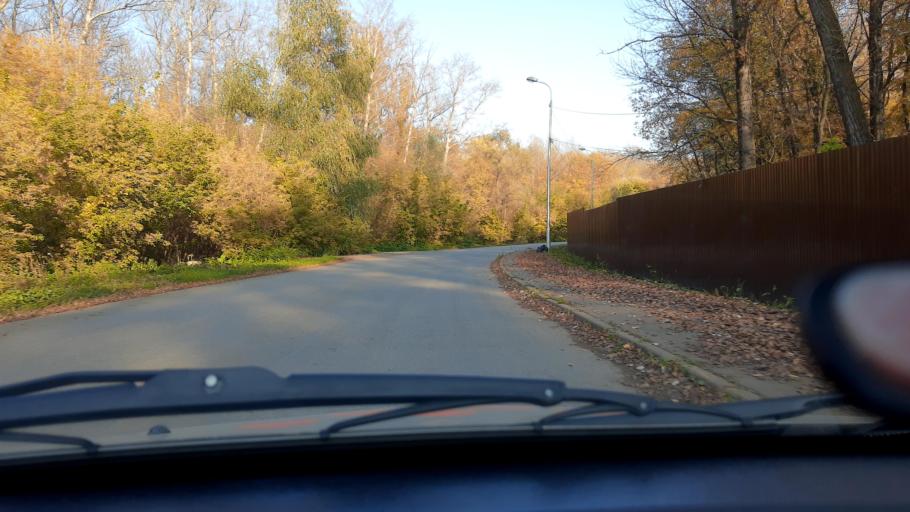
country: RU
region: Bashkortostan
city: Ufa
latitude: 54.8123
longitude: 56.0428
